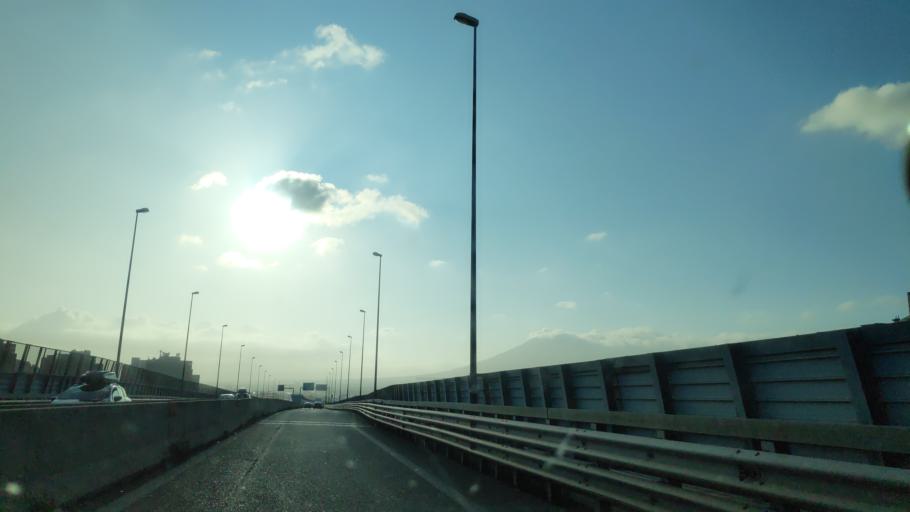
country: IT
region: Campania
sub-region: Provincia di Napoli
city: Napoli
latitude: 40.8630
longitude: 14.2780
